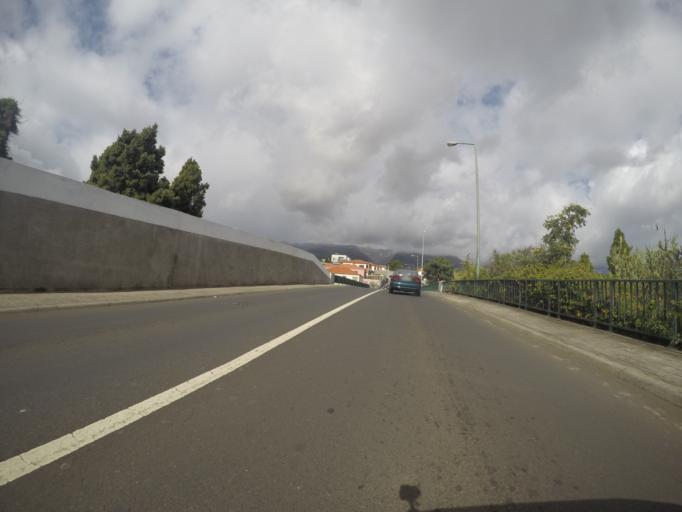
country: PT
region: Madeira
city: Camara de Lobos
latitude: 32.6520
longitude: -16.9423
